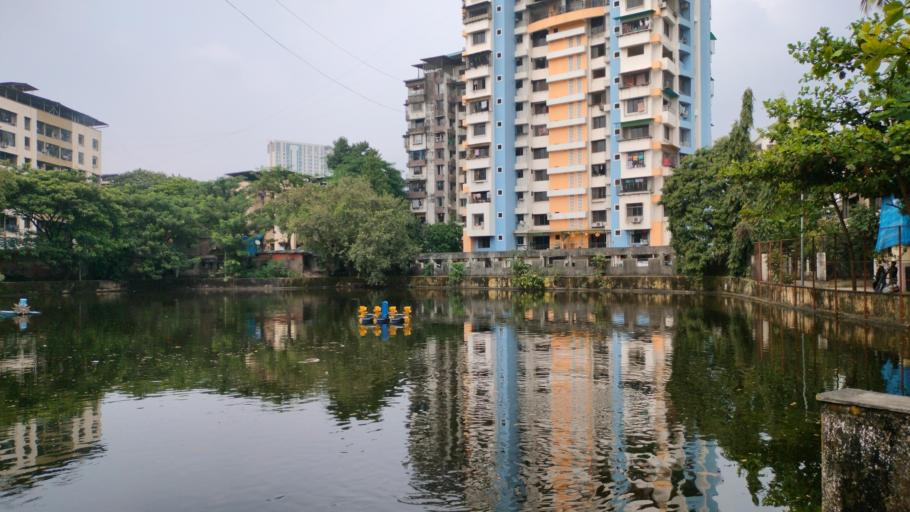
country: IN
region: Maharashtra
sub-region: Thane
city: Thane
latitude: 19.2047
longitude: 72.9750
